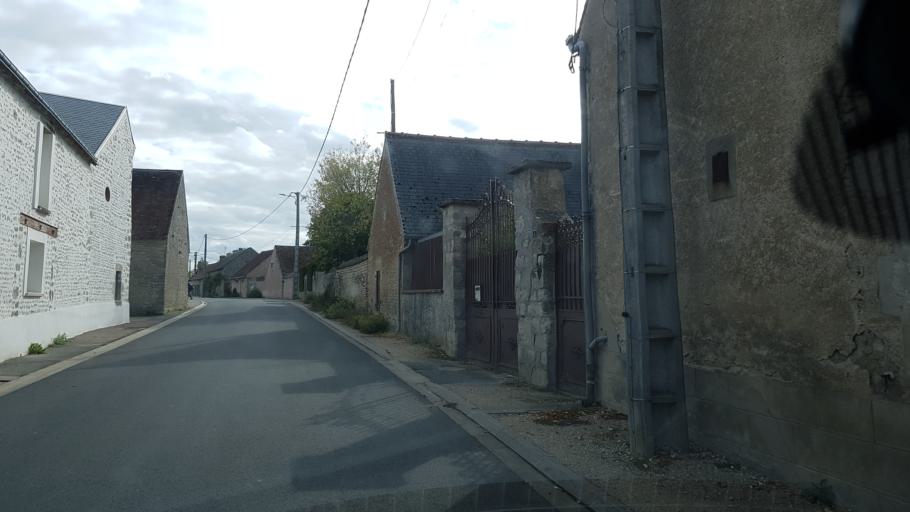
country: FR
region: Centre
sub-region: Departement du Loiret
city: Pithiviers-le-Vieil
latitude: 48.1035
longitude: 2.1932
